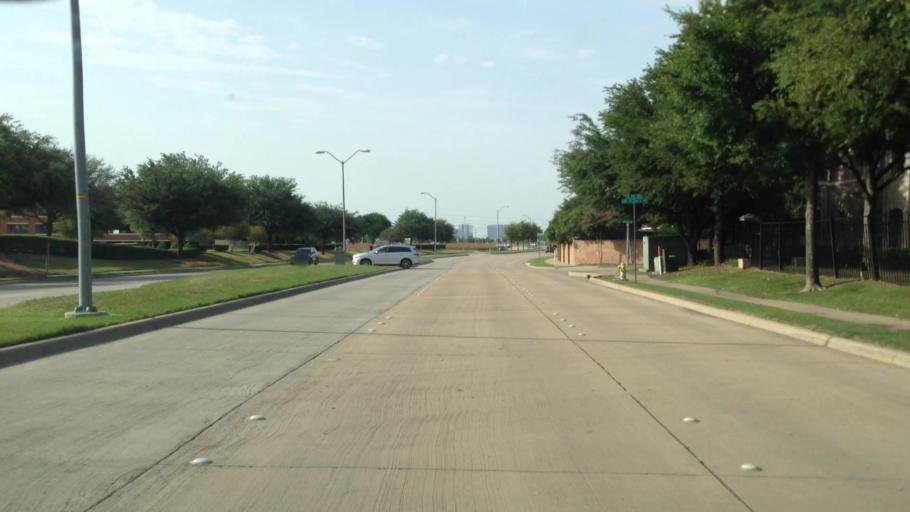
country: US
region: Texas
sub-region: Denton County
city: The Colony
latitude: 33.0493
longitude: -96.8265
